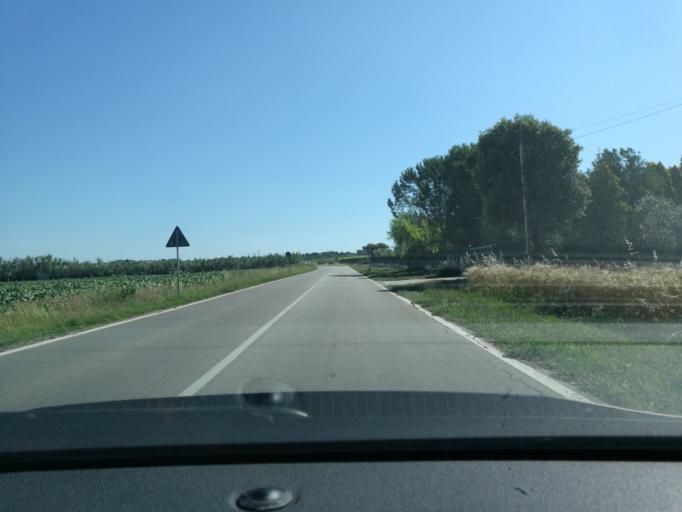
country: IT
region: Abruzzo
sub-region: Provincia di Chieti
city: Vasto
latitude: 42.1594
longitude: 14.7027
